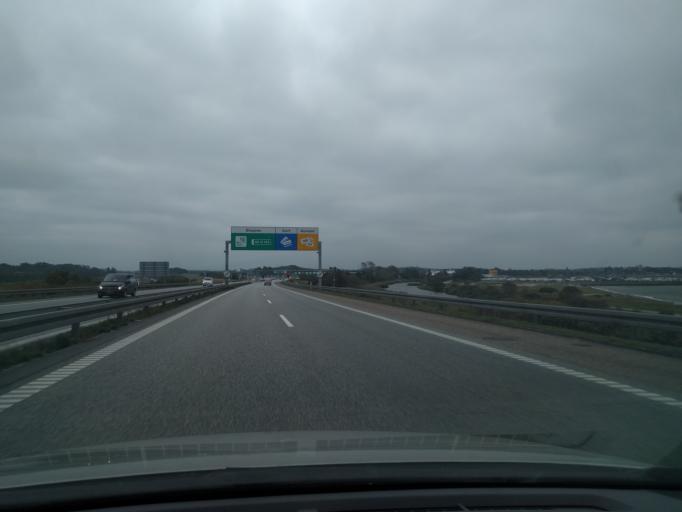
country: DK
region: Zealand
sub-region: Slagelse Kommune
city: Korsor
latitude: 55.3491
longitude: 11.0964
